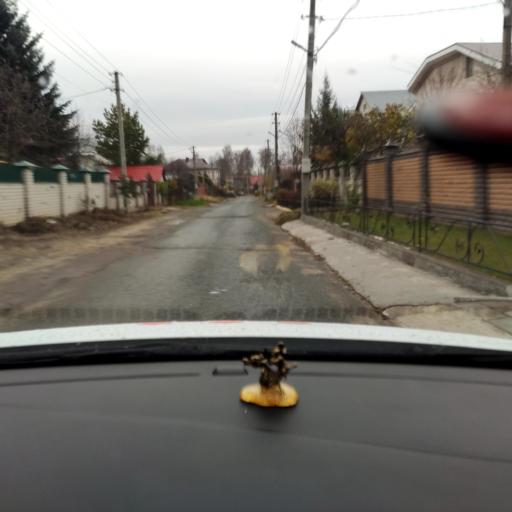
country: RU
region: Tatarstan
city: Vysokaya Gora
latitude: 55.8442
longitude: 49.2388
